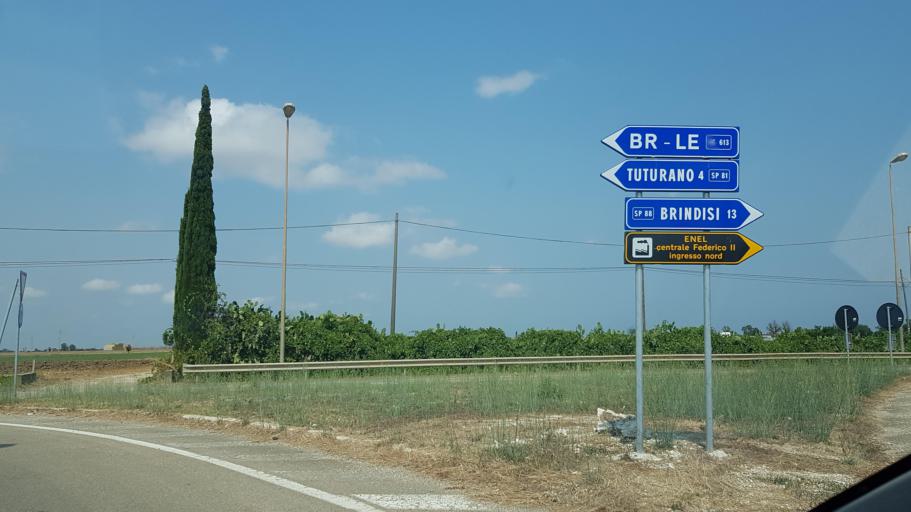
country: IT
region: Apulia
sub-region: Provincia di Brindisi
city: Tuturano
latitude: 40.5616
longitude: 18.0083
